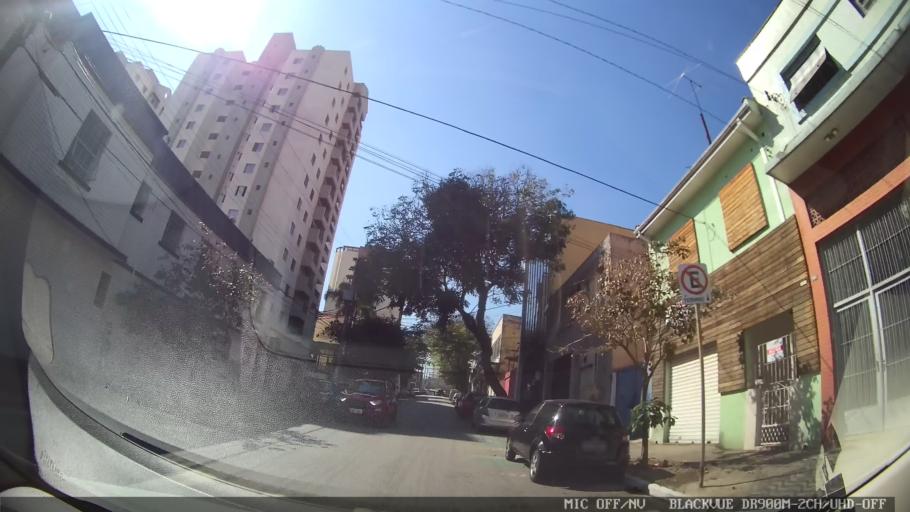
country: BR
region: Sao Paulo
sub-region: Sao Paulo
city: Sao Paulo
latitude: -23.5093
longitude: -46.6598
